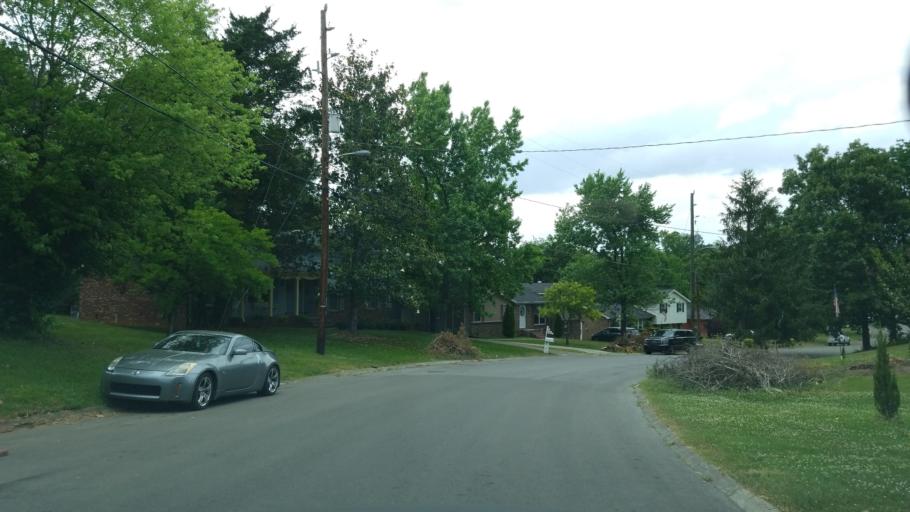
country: US
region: Tennessee
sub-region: Rutherford County
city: La Vergne
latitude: 36.0797
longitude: -86.6191
